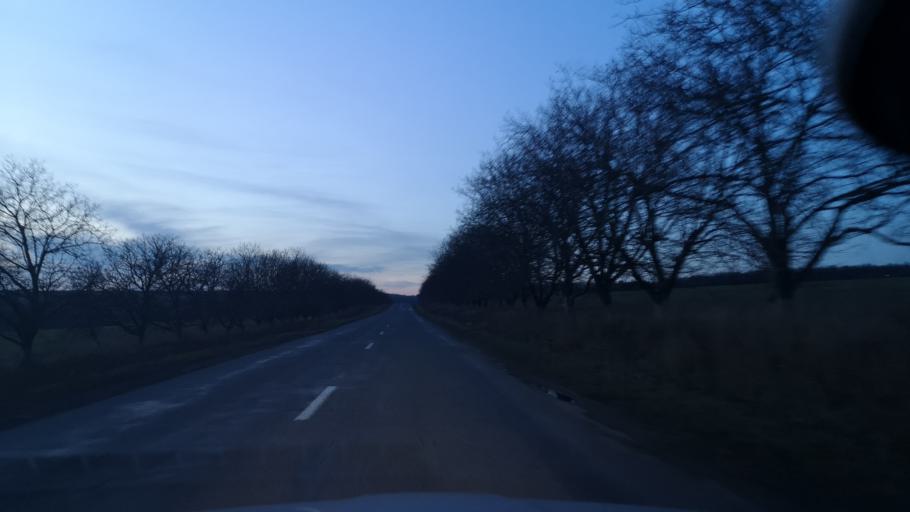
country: MD
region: Orhei
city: Orhei
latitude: 47.2888
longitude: 28.8185
